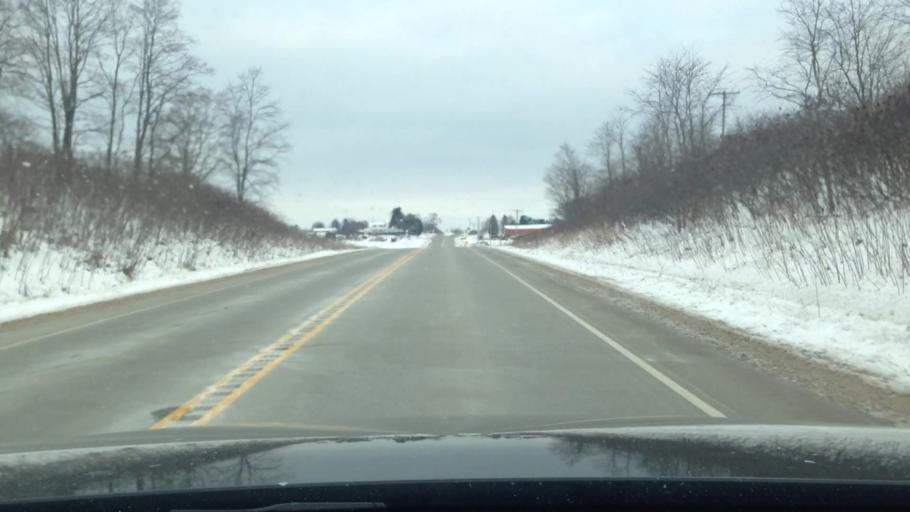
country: US
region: Wisconsin
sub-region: Walworth County
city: Lake Geneva
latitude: 42.5385
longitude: -88.4429
